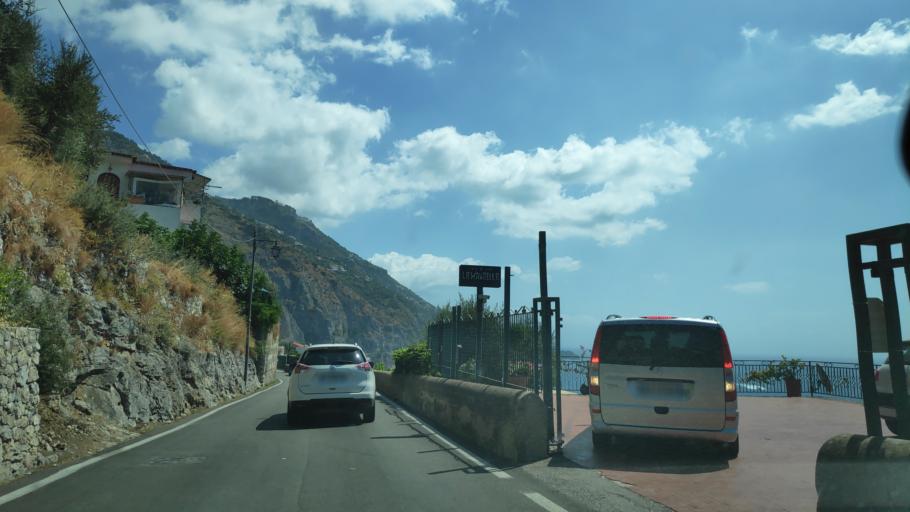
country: IT
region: Campania
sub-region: Provincia di Salerno
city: Praiano
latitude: 40.6116
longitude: 14.5377
